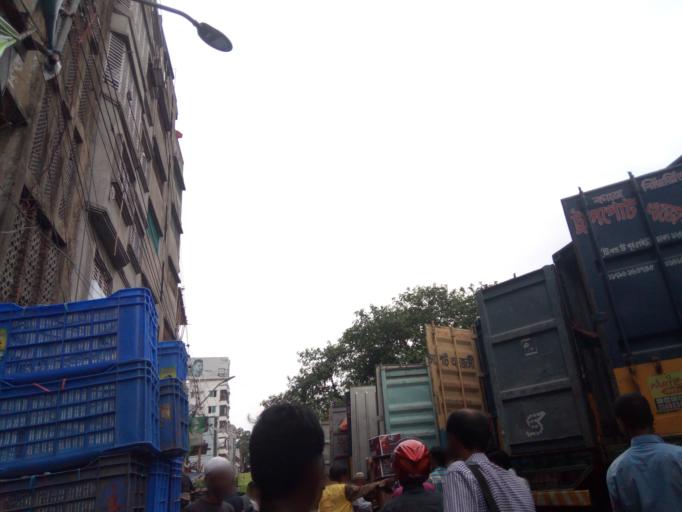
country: BD
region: Dhaka
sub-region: Dhaka
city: Dhaka
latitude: 23.7091
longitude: 90.4036
